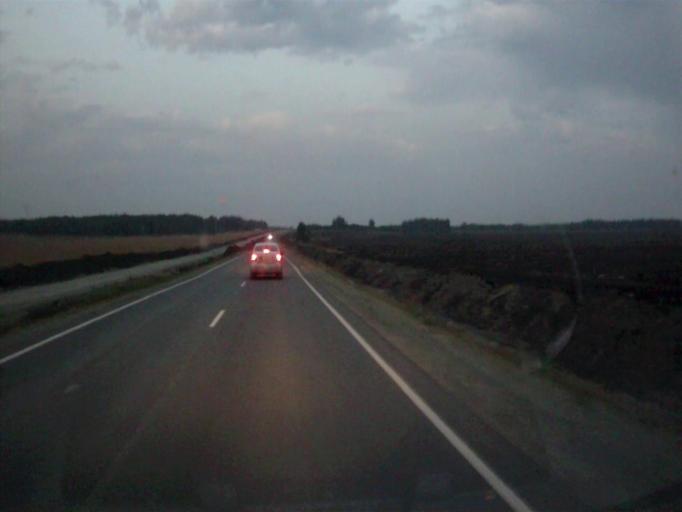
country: RU
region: Chelyabinsk
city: Timiryazevskiy
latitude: 55.2079
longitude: 60.8148
